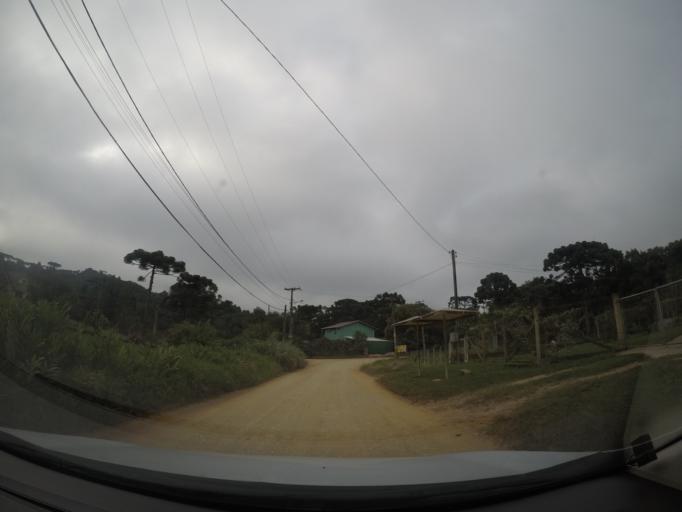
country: BR
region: Parana
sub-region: Colombo
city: Colombo
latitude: -25.3216
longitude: -49.2532
